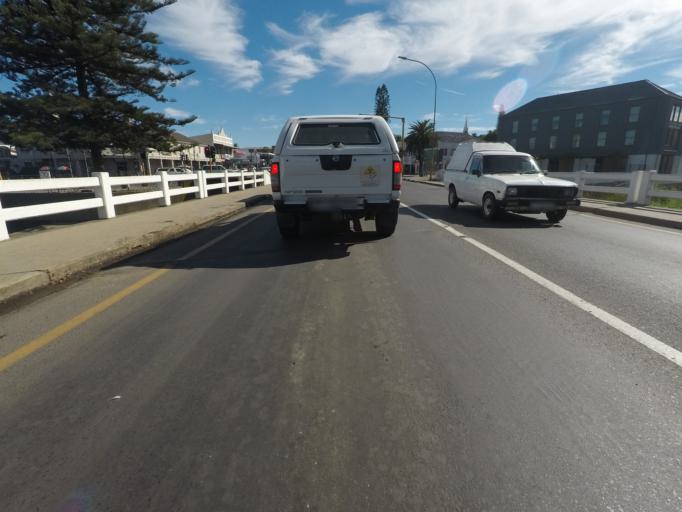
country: ZA
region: Western Cape
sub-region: West Coast District Municipality
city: Malmesbury
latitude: -33.4662
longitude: 18.7289
